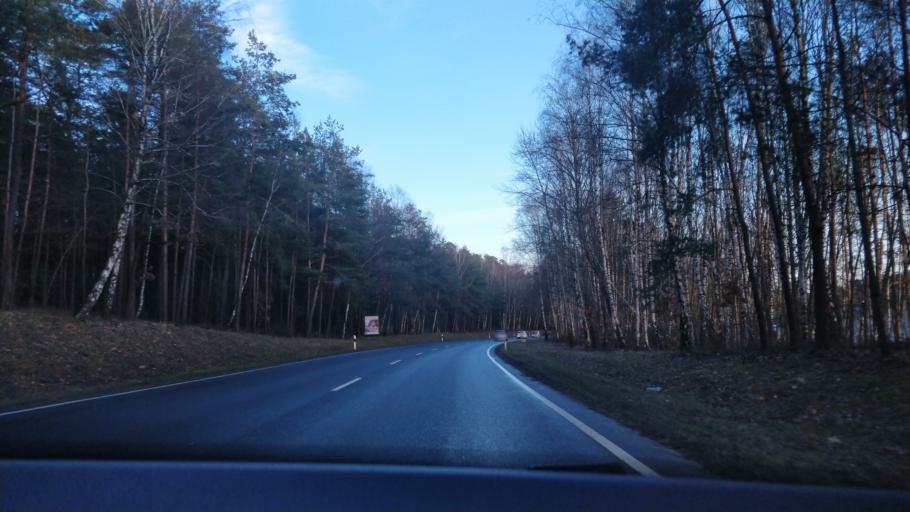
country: DE
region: Bavaria
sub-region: Upper Palatinate
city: Parkstein
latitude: 49.6895
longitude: 12.1004
